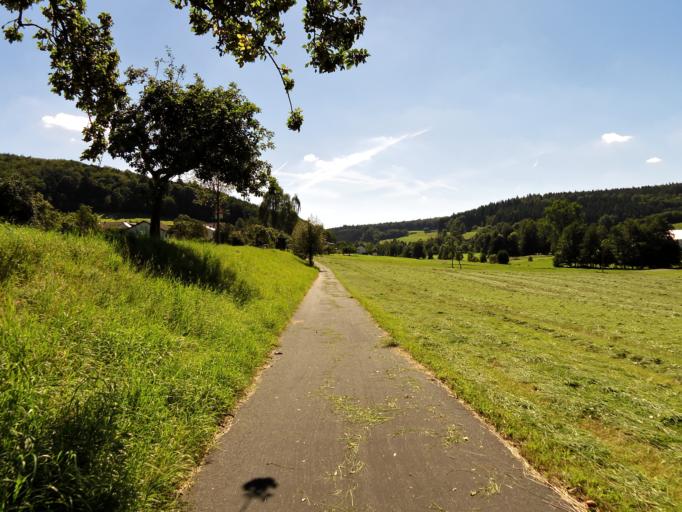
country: DE
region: Hesse
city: Reichelsheim
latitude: 49.6467
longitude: 8.8897
